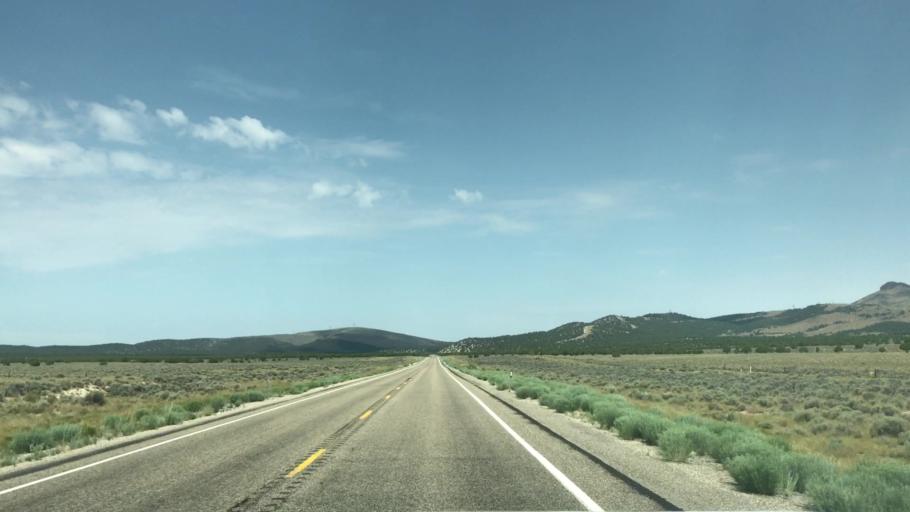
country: US
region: Nevada
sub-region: White Pine County
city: Ely
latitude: 39.3638
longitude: -115.0508
